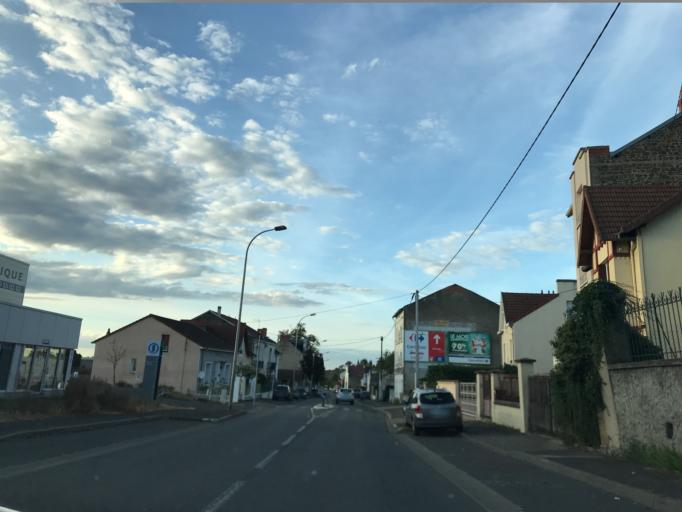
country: FR
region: Auvergne
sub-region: Departement de l'Allier
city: Abrest
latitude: 46.1130
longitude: 3.4405
